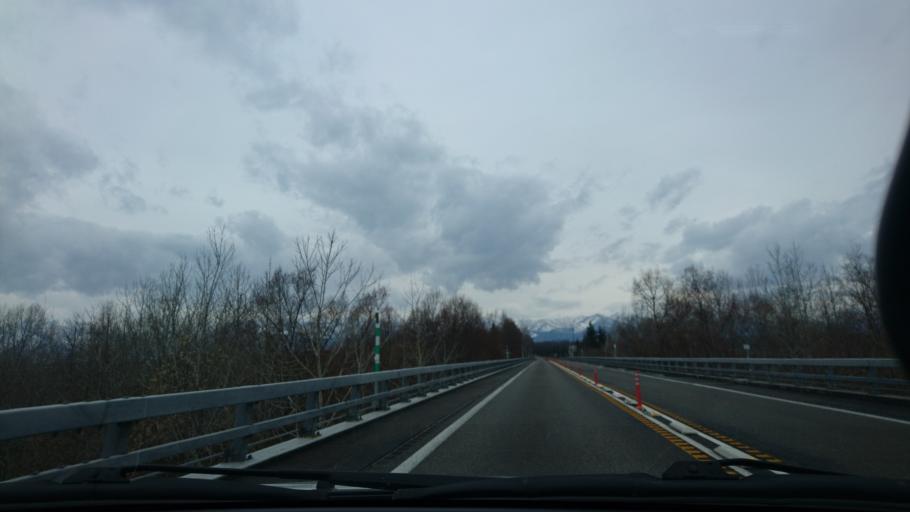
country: JP
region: Hokkaido
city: Otofuke
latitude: 42.9786
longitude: 142.9492
